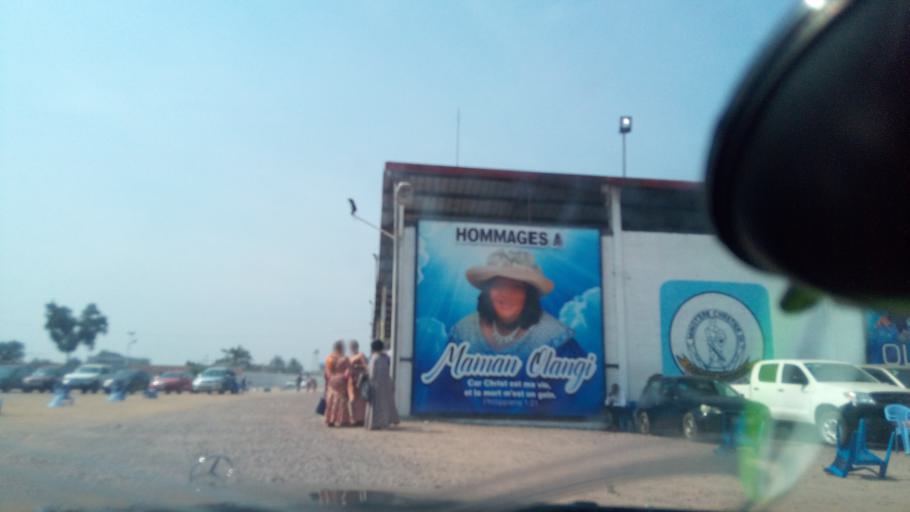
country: CD
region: Kinshasa
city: Masina
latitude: -4.3730
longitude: 15.3492
